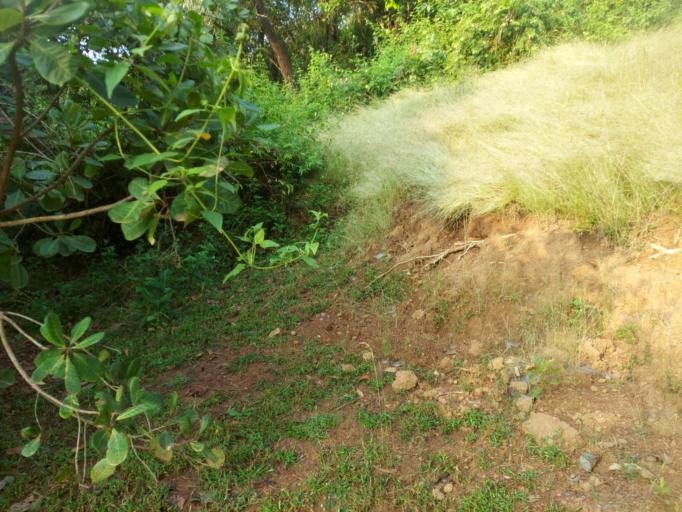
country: IN
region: Maharashtra
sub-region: Sindhudurg
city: Kudal
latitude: 16.0387
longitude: 73.6738
